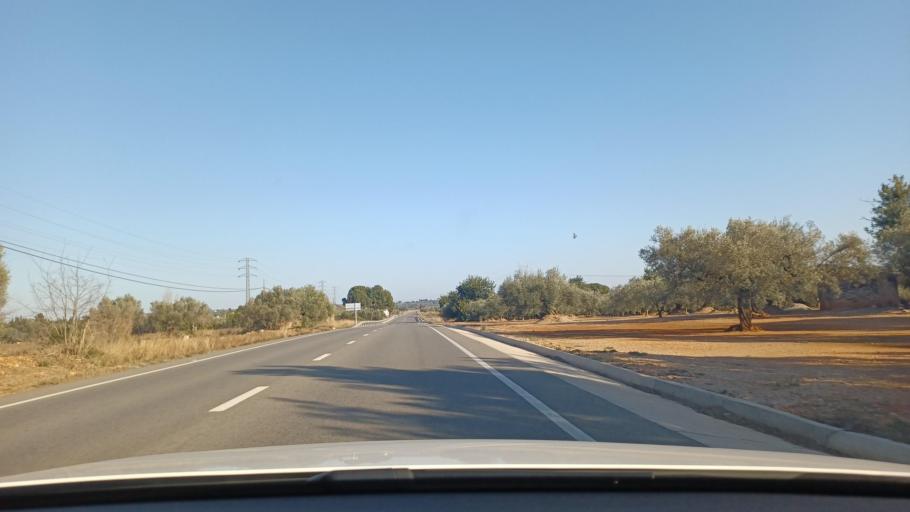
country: ES
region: Catalonia
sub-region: Provincia de Tarragona
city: Santa Barbara
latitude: 40.7170
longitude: 0.5106
